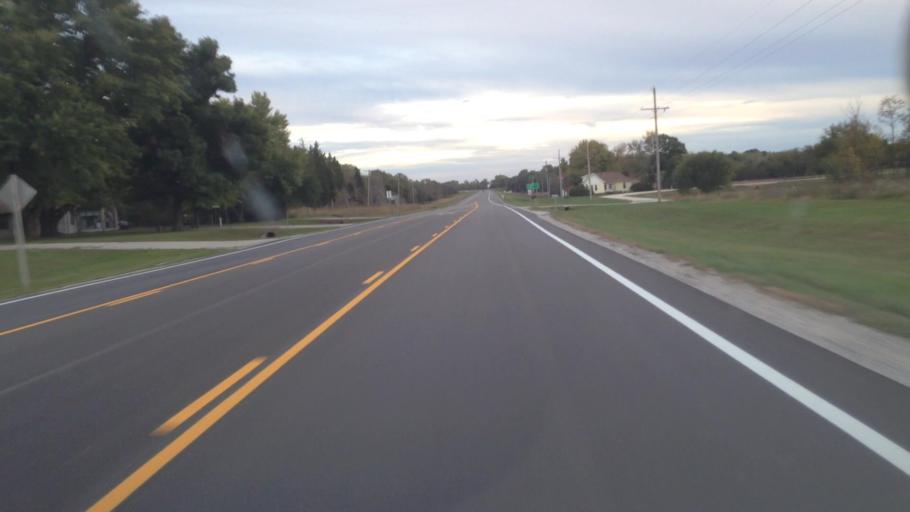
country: US
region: Kansas
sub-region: Franklin County
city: Ottawa
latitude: 38.4858
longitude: -95.2675
